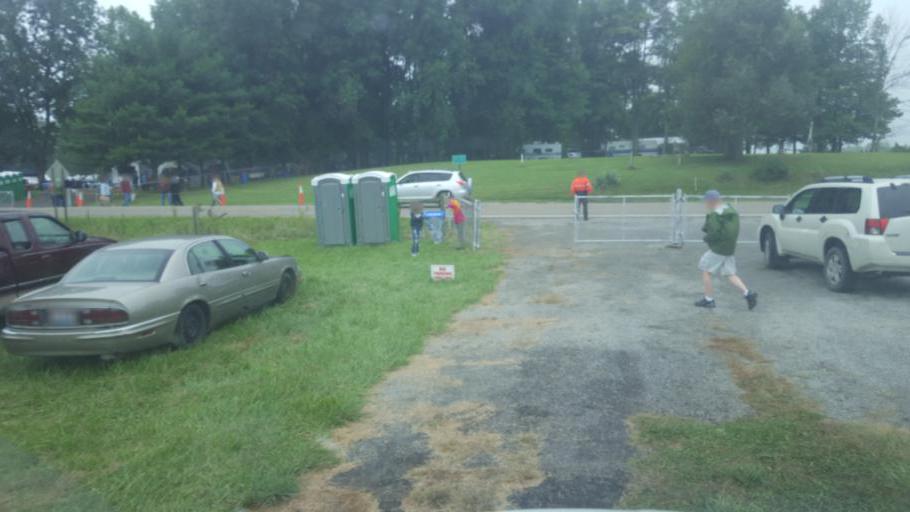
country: US
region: Ohio
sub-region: Licking County
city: Johnstown
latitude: 40.1579
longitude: -82.6345
